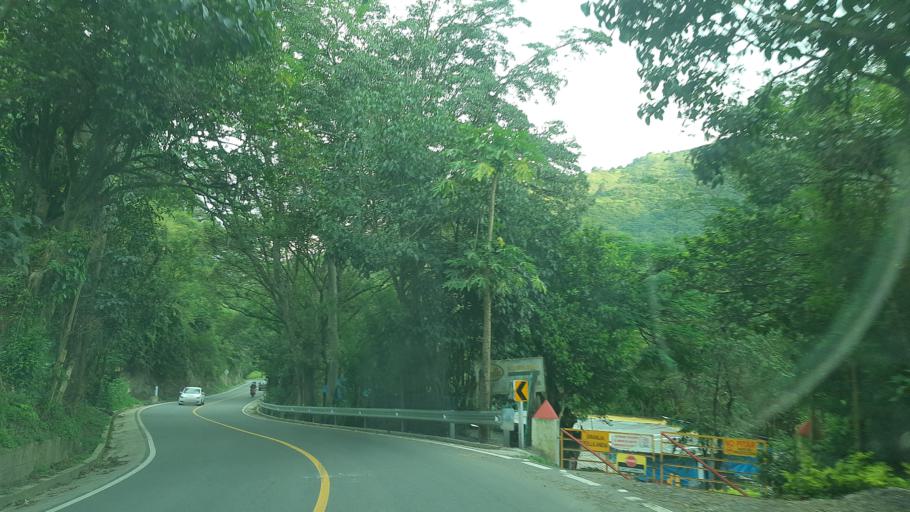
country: CO
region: Boyaca
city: Somondoco
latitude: 5.0089
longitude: -73.4233
